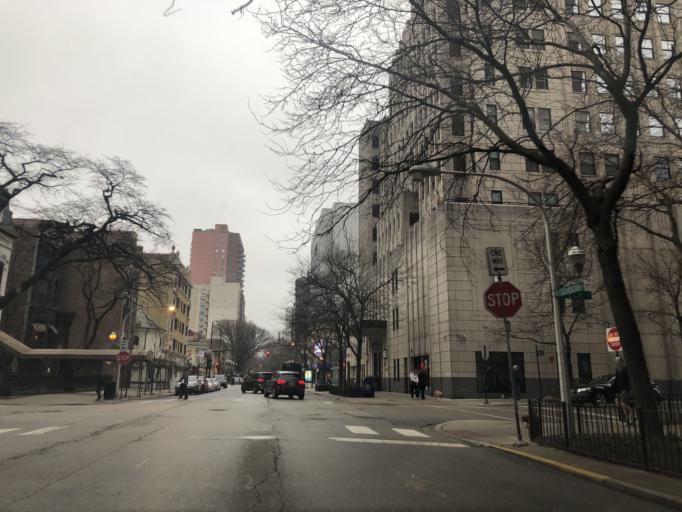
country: US
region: Illinois
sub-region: Cook County
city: Chicago
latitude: 41.9029
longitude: -87.6299
